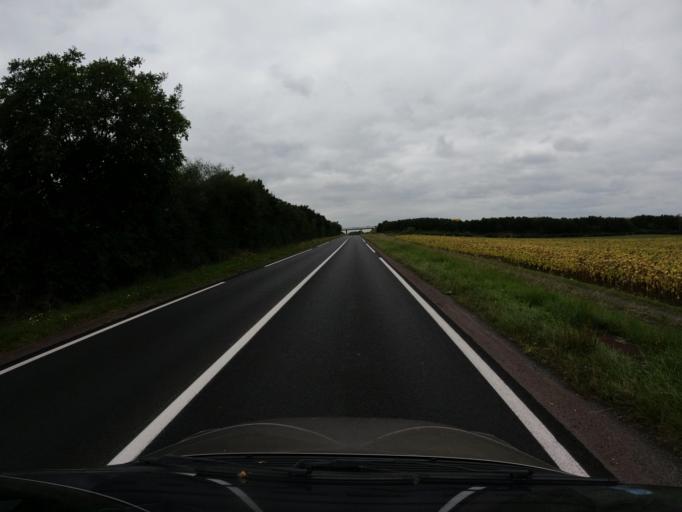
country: FR
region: Pays de la Loire
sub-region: Departement de la Vendee
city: Benet
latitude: 46.3923
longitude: -0.6408
